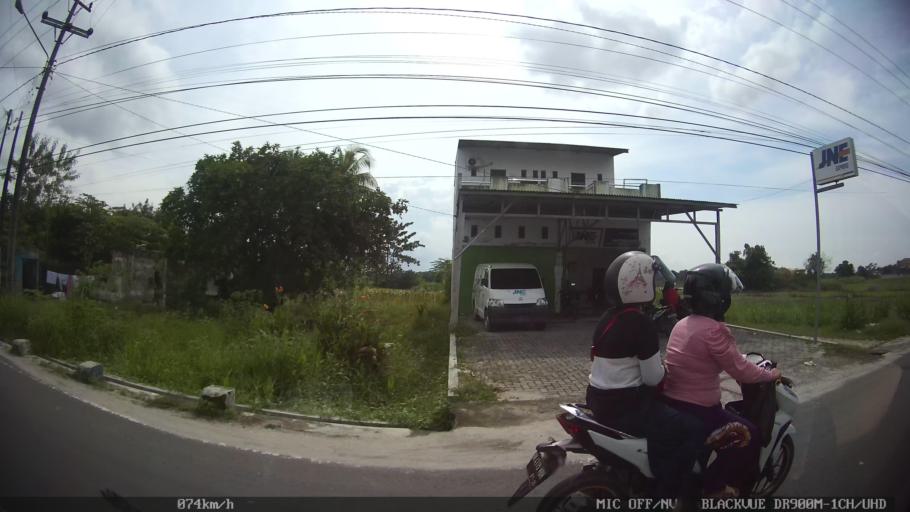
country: ID
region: North Sumatra
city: Percut
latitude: 3.5865
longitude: 98.8606
